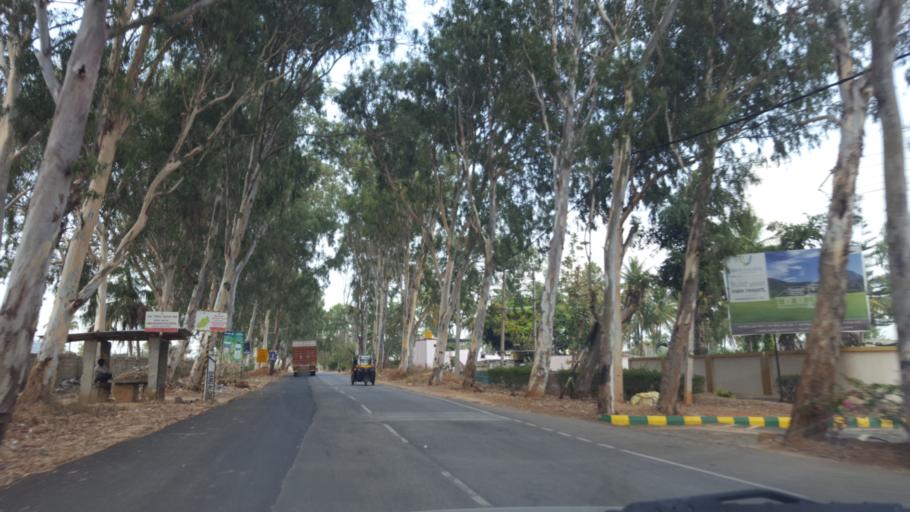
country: IN
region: Karnataka
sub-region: Chikkaballapur
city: Chik Ballapur
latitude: 13.3493
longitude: 77.6868
